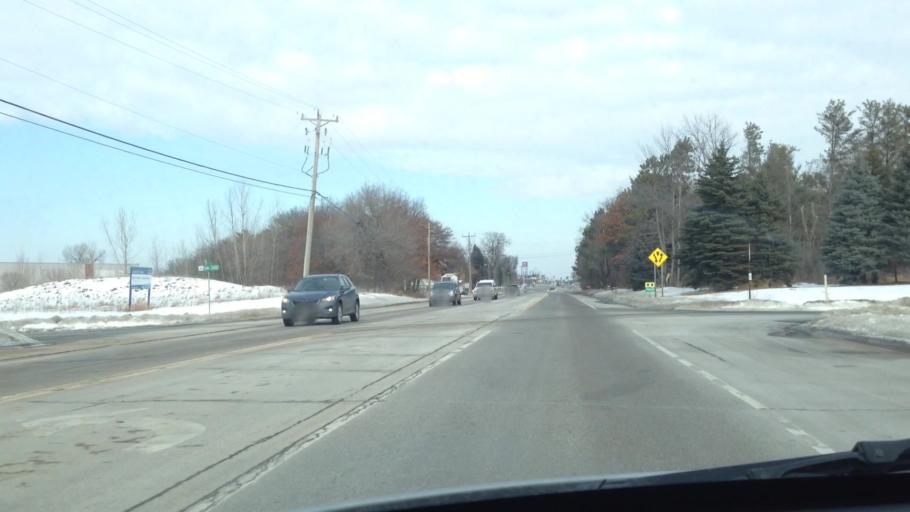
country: US
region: Minnesota
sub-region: Anoka County
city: Lino Lakes
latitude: 45.1728
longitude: -93.1179
